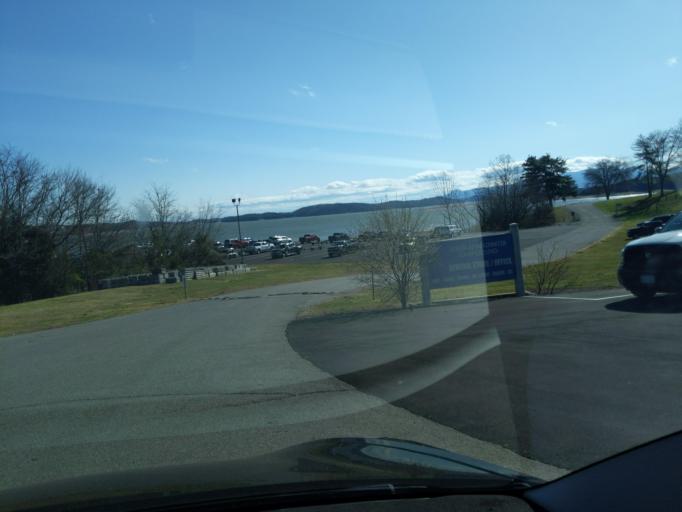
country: US
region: Tennessee
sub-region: Sevier County
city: Sevierville
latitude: 35.9578
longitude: -83.5360
